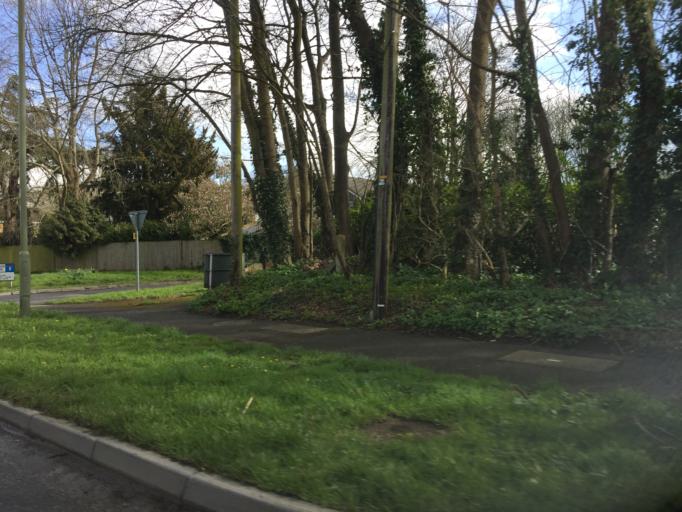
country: GB
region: England
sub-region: Hampshire
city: Compton
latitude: 51.0090
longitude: -1.3427
